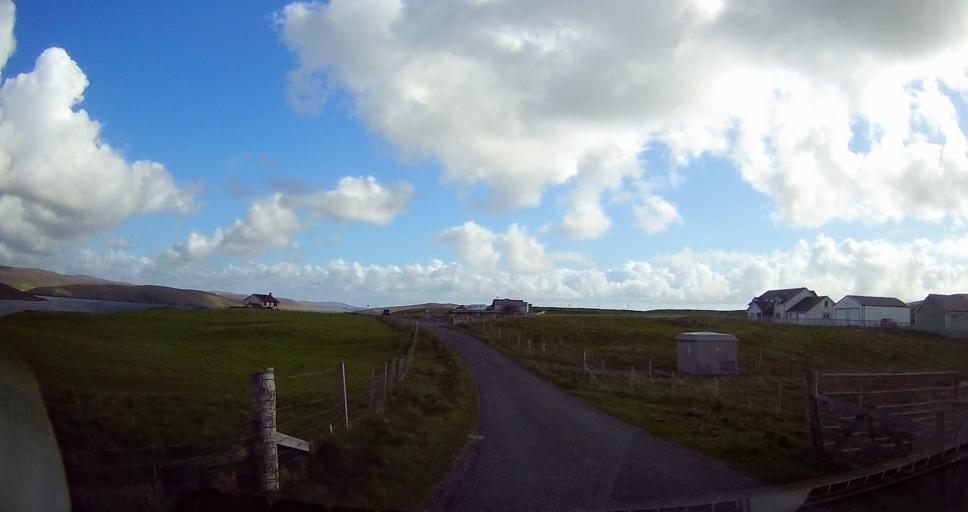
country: GB
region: Scotland
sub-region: Shetland Islands
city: Lerwick
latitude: 60.3648
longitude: -1.3825
